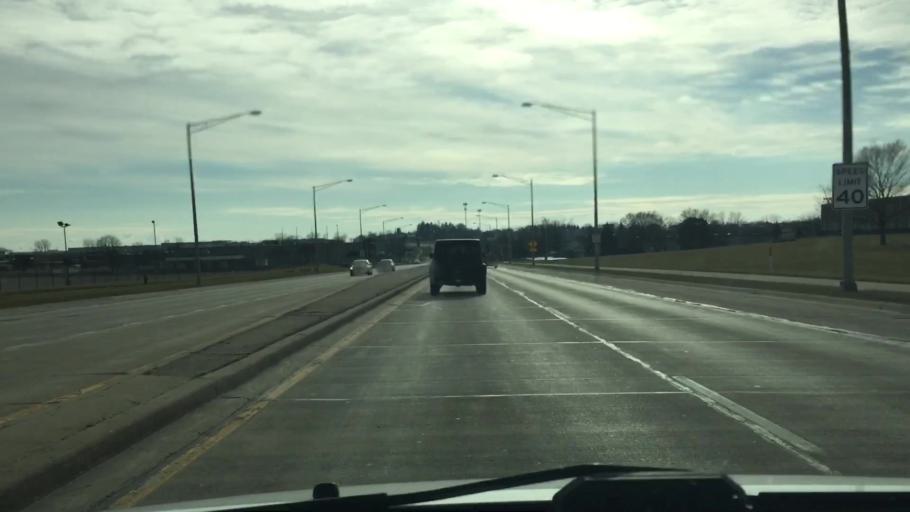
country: US
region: Illinois
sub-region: Kane County
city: Saint Charles
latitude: 41.9158
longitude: -88.2766
